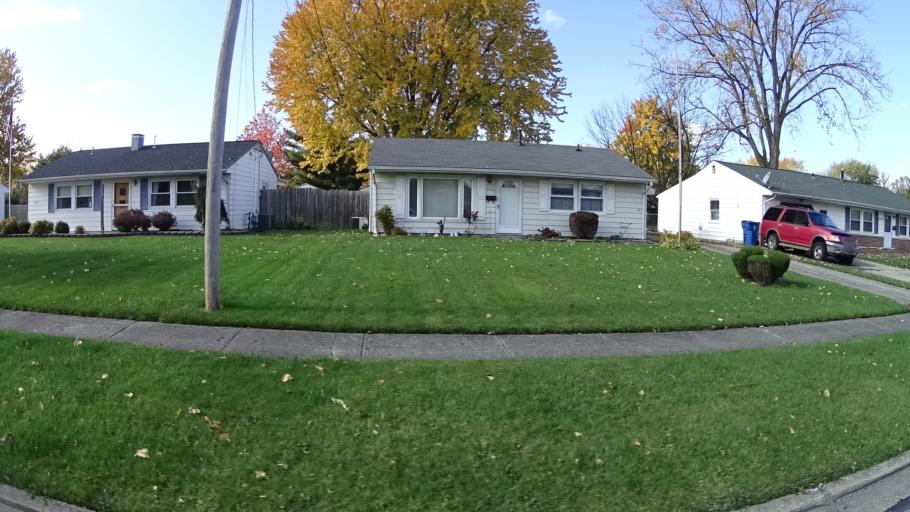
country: US
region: Ohio
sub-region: Lorain County
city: Lorain
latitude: 41.4478
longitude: -82.2156
